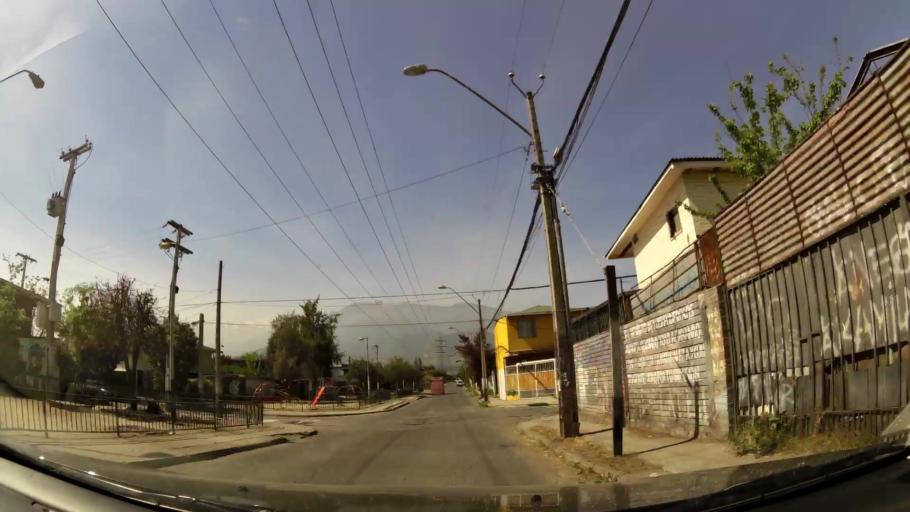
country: CL
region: Santiago Metropolitan
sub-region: Provincia de Cordillera
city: Puente Alto
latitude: -33.5694
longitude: -70.5698
